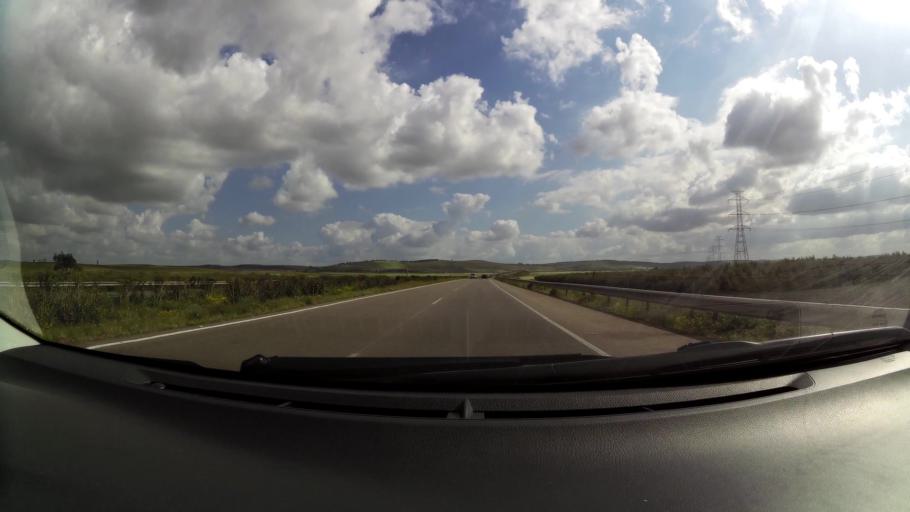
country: MA
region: Chaouia-Ouardigha
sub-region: Settat Province
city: Settat
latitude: 33.1044
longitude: -7.5830
